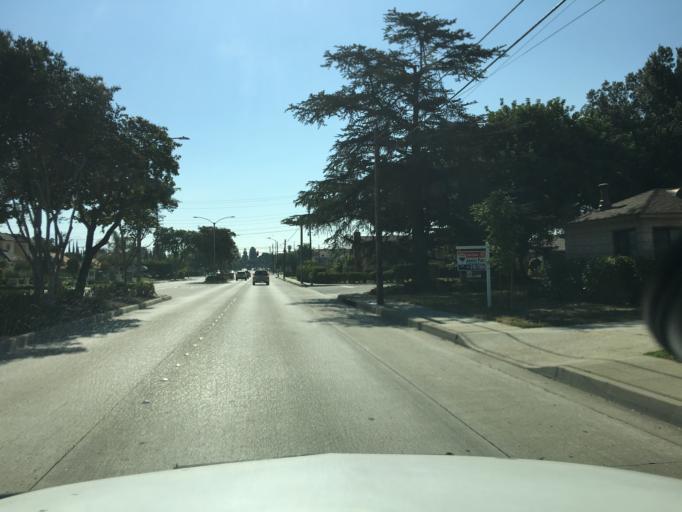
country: US
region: California
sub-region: Los Angeles County
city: North El Monte
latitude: 34.1076
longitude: -118.0401
